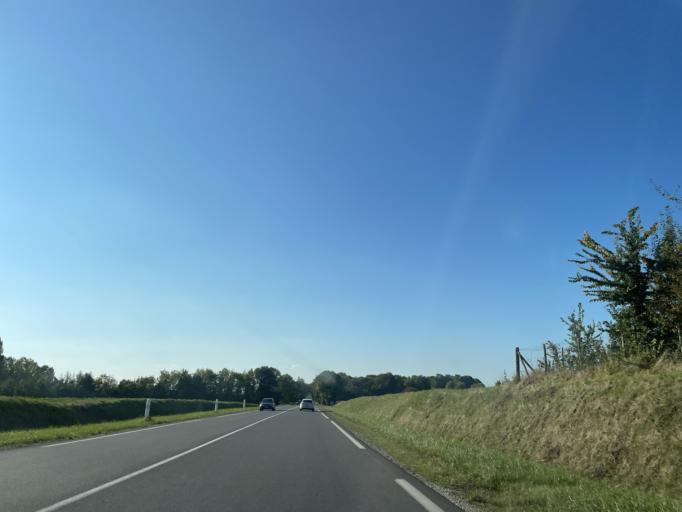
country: FR
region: Ile-de-France
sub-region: Departement de Seine-et-Marne
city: La Celle-sur-Morin
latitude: 48.8364
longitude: 2.9852
